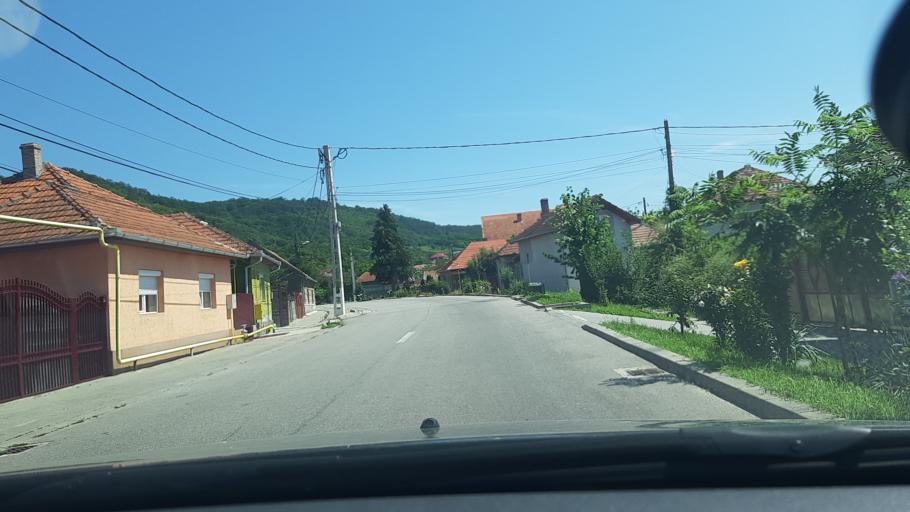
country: RO
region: Hunedoara
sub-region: Oras Hateg
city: Hateg
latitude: 45.6146
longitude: 22.9544
